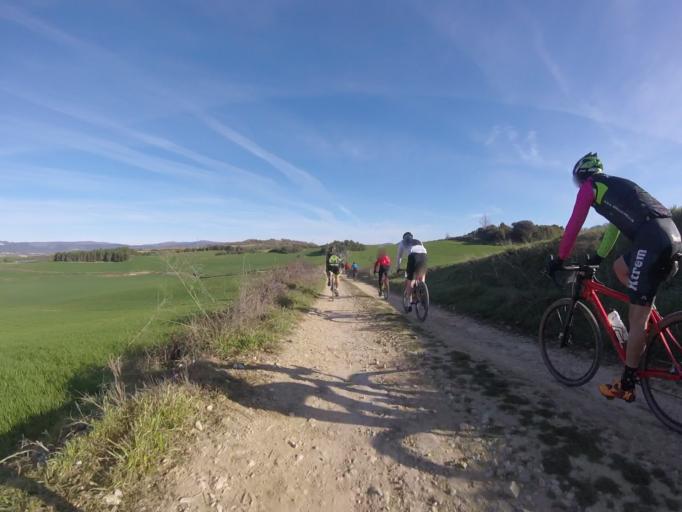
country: ES
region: Navarre
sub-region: Provincia de Navarra
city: Villatuerta
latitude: 42.6601
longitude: -1.9660
